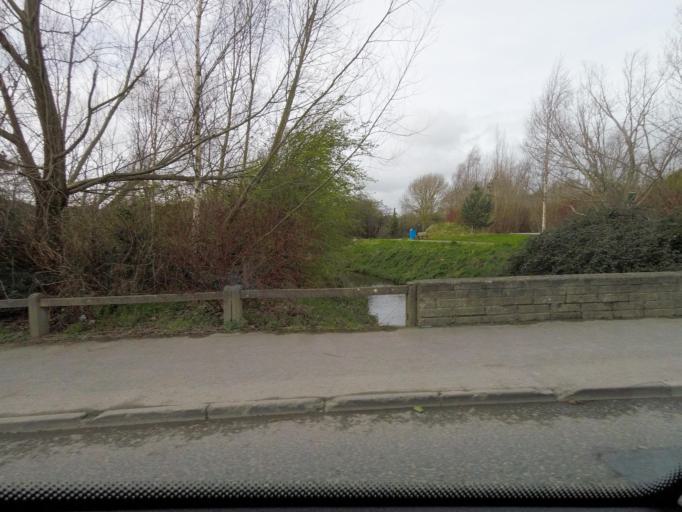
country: IE
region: Leinster
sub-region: Kildare
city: Naas
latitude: 53.2134
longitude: -6.6507
